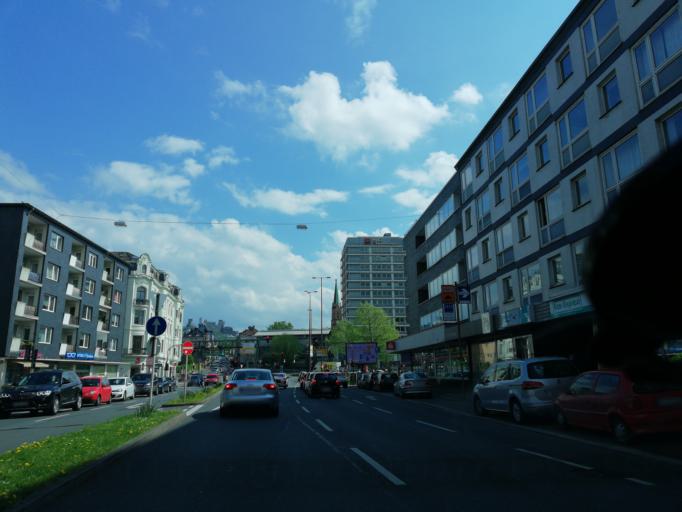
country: DE
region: North Rhine-Westphalia
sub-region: Regierungsbezirk Dusseldorf
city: Wuppertal
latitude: 51.2539
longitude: 7.1324
